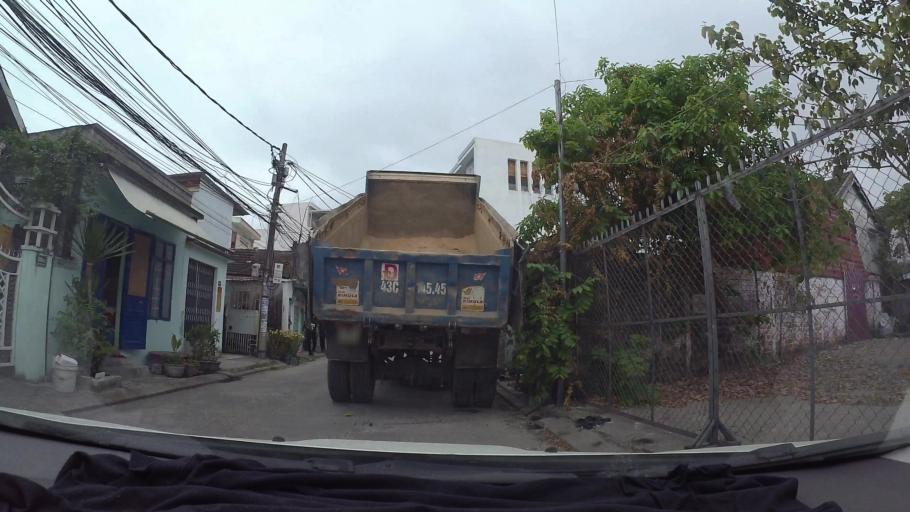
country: VN
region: Da Nang
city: Lien Chieu
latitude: 16.0706
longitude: 108.1528
